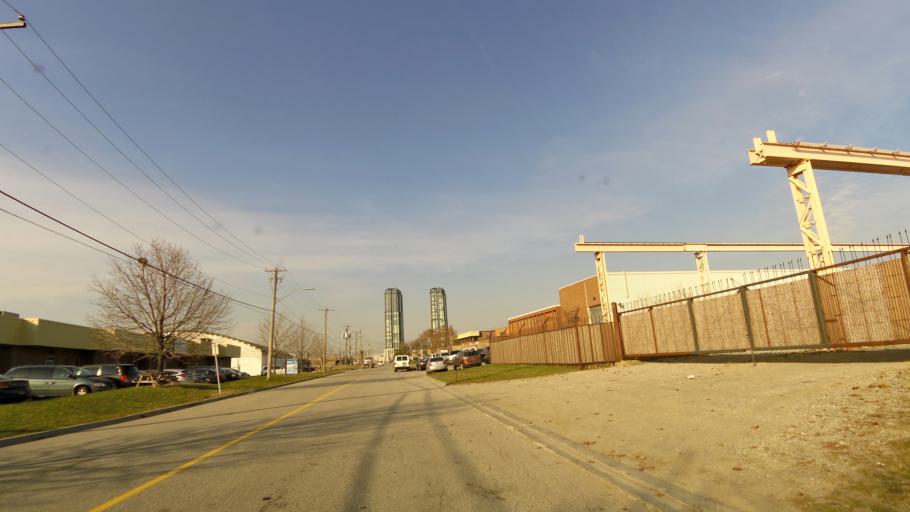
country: CA
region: Ontario
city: Concord
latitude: 43.7889
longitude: -79.5195
